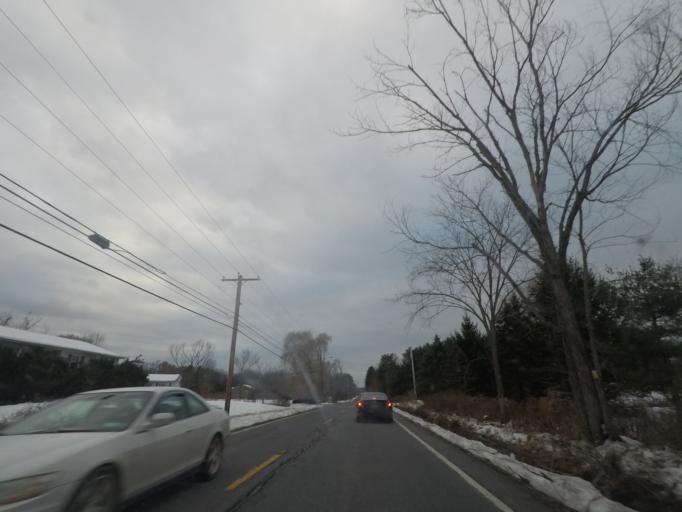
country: US
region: New York
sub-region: Ulster County
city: New Paltz
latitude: 41.7056
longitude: -74.0934
